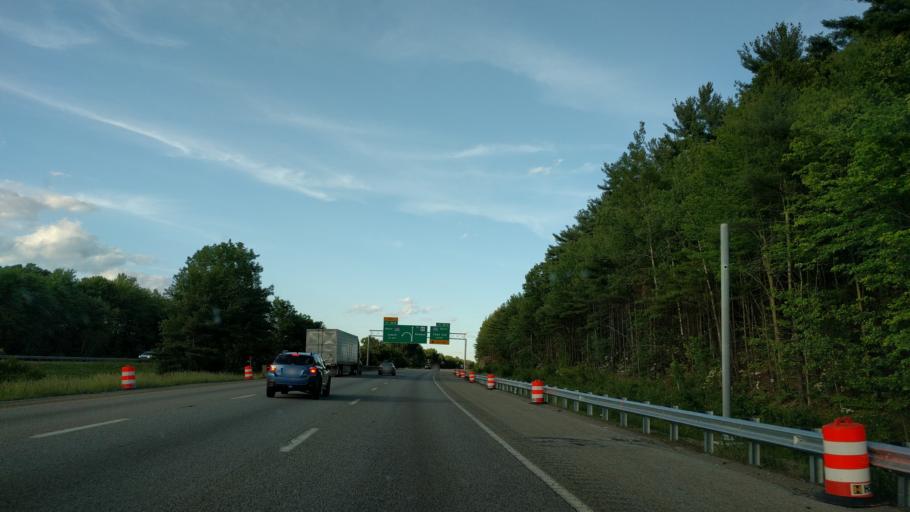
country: US
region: Massachusetts
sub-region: Worcester County
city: Berlin
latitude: 42.3580
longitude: -71.6039
